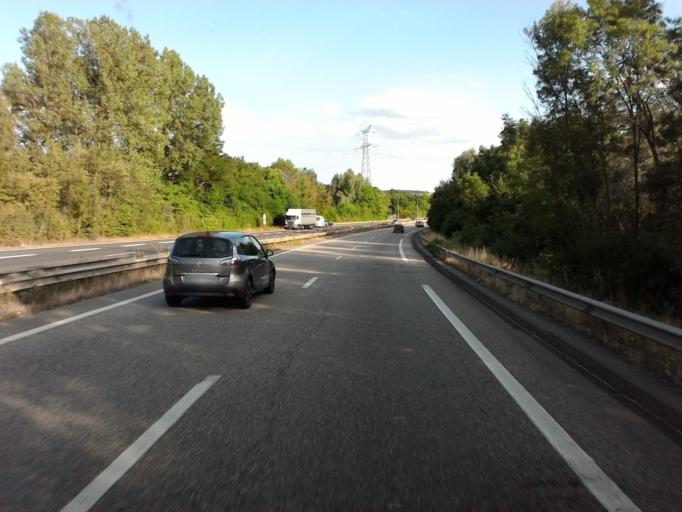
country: FR
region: Lorraine
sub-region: Departement de Meurthe-et-Moselle
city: Richardmenil
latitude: 48.5872
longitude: 6.1760
